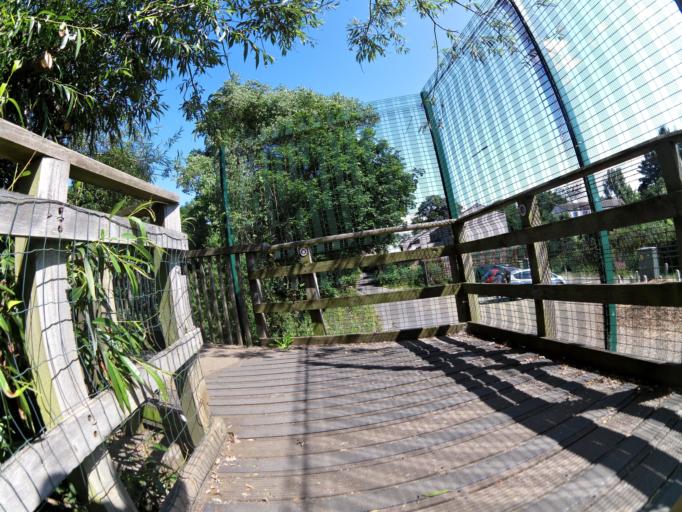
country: GB
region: Scotland
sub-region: Edinburgh
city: Colinton
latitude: 55.9282
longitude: -3.2554
